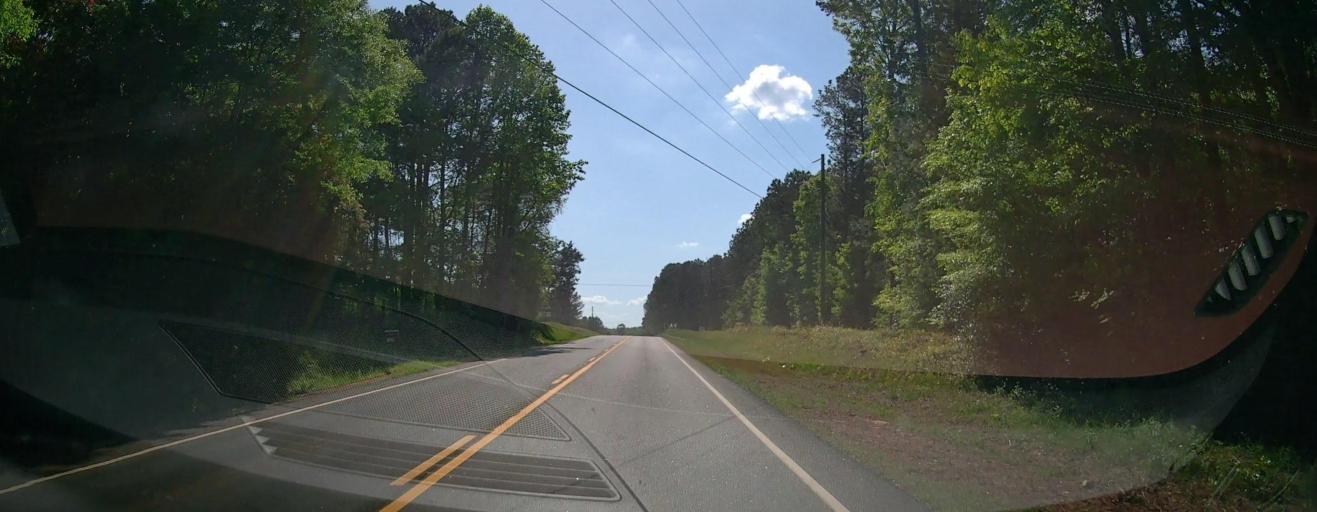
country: US
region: Georgia
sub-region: Morgan County
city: Madison
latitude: 33.6083
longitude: -83.3755
